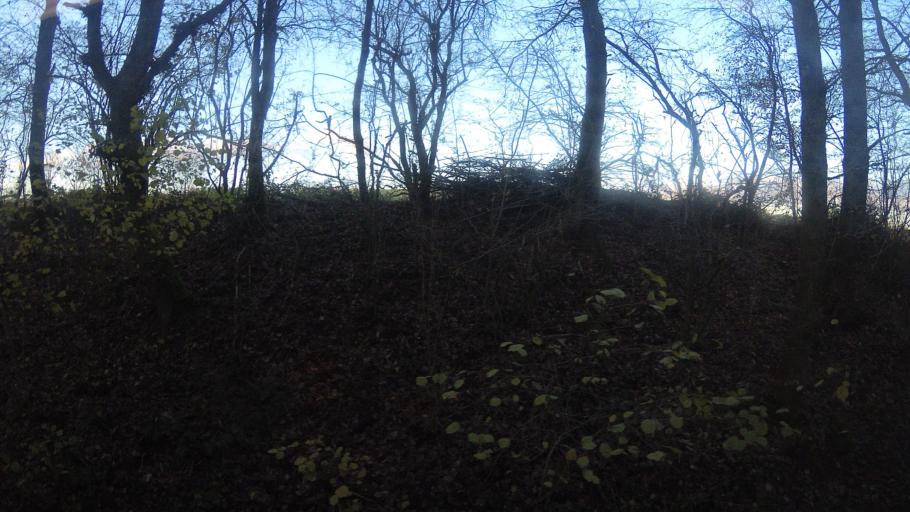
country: DE
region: Saarland
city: Ottweiler
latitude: 49.4169
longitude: 7.1949
